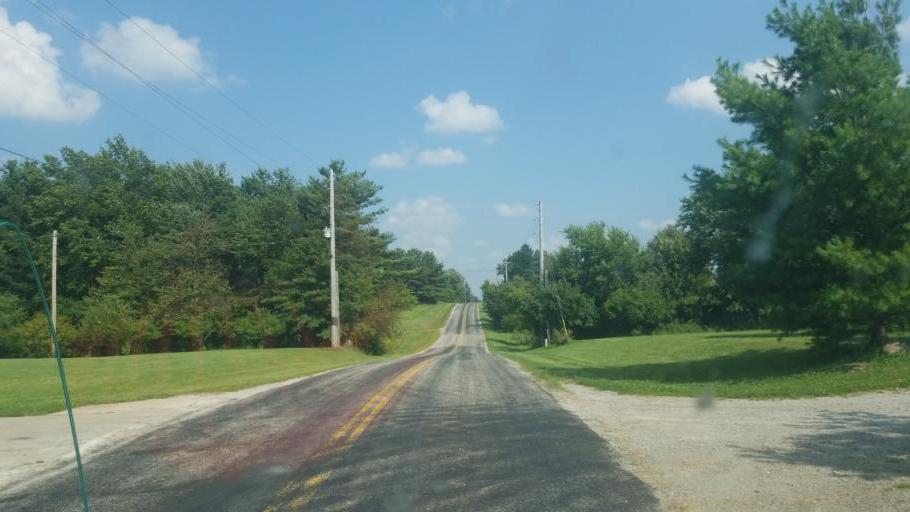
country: US
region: Ohio
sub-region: Lorain County
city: Wellington
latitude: 41.0578
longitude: -82.2502
